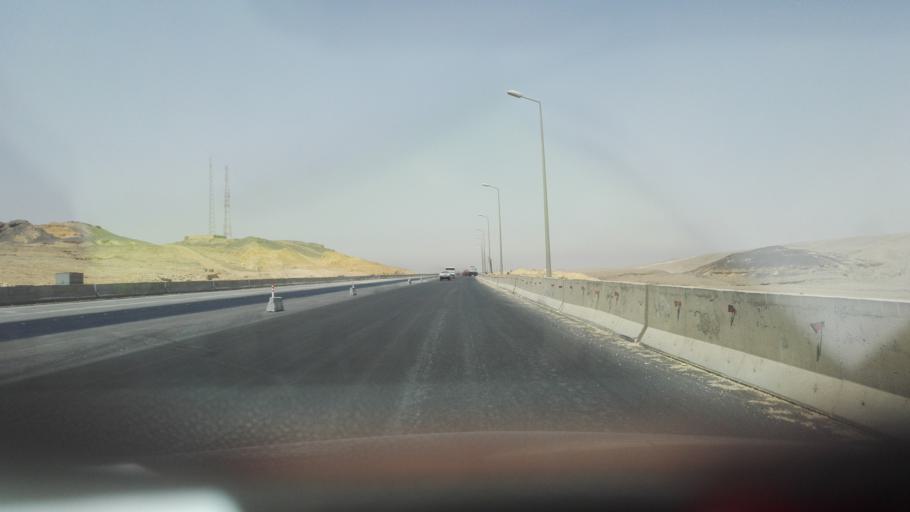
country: EG
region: As Suways
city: Ain Sukhna
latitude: 29.6975
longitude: 32.1054
